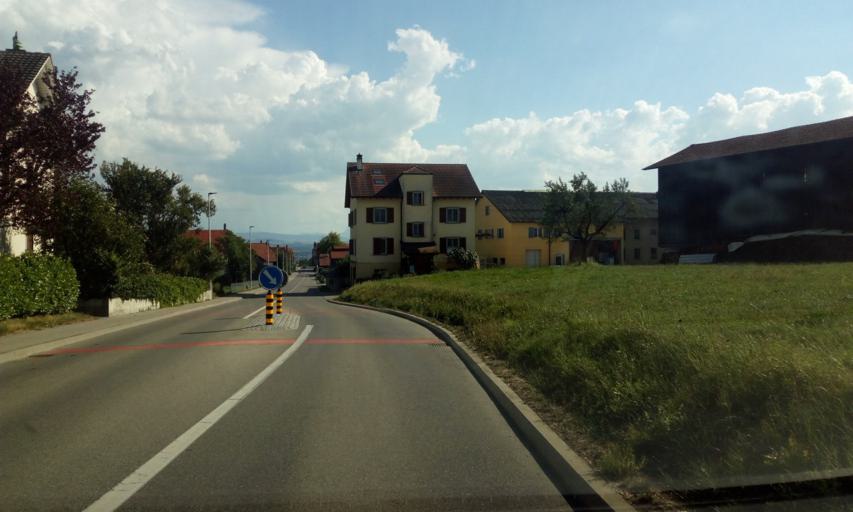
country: CH
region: Fribourg
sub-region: Broye District
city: Domdidier
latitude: 46.8954
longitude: 6.9753
